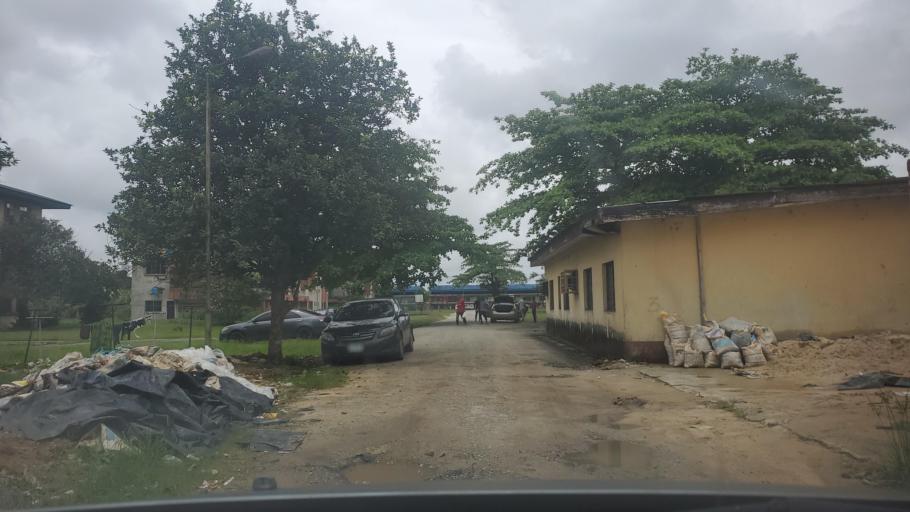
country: NG
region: Rivers
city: Emuoha
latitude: 4.8991
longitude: 6.9234
